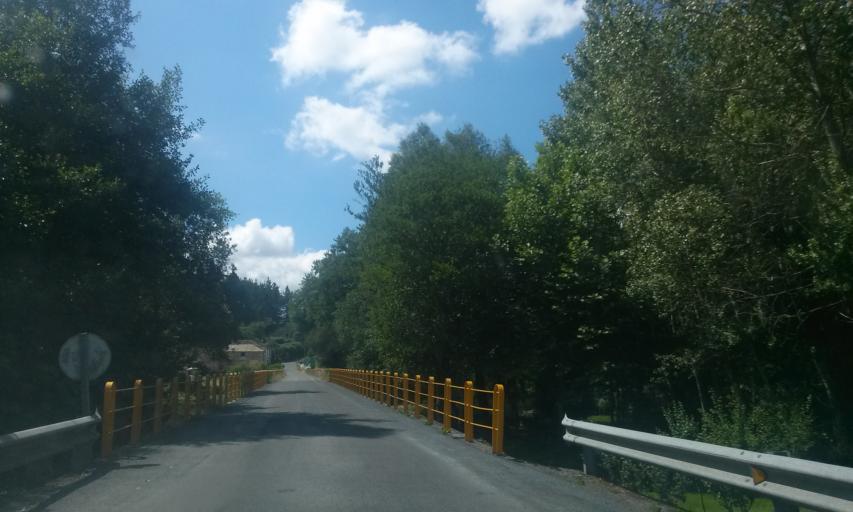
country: ES
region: Galicia
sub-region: Provincia de Lugo
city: Rabade
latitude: 43.1159
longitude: -7.6559
